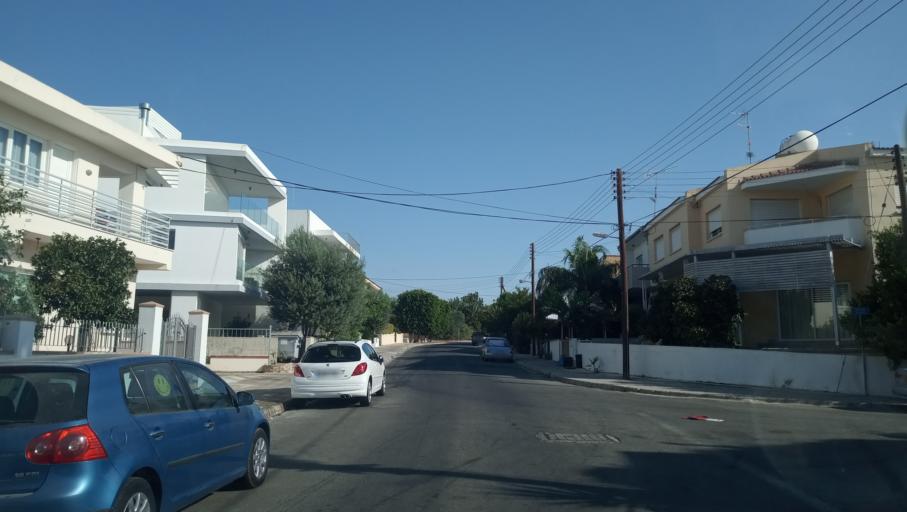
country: CY
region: Lefkosia
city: Nicosia
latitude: 35.1445
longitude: 33.3947
